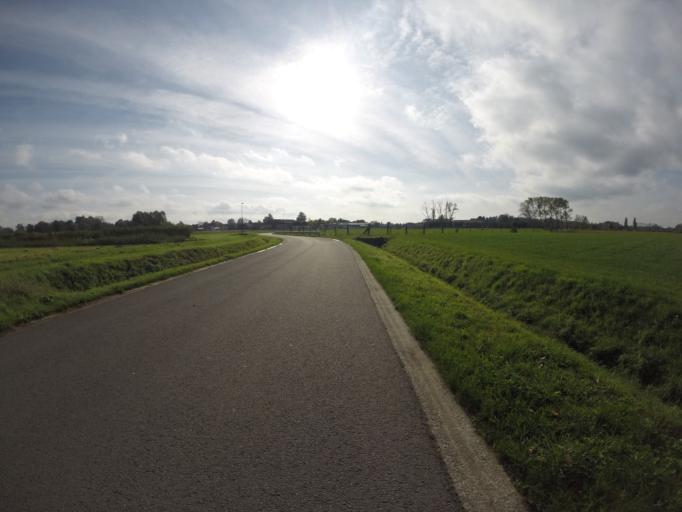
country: BE
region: Flanders
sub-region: Provincie Oost-Vlaanderen
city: Knesselare
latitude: 51.1297
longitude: 3.4176
